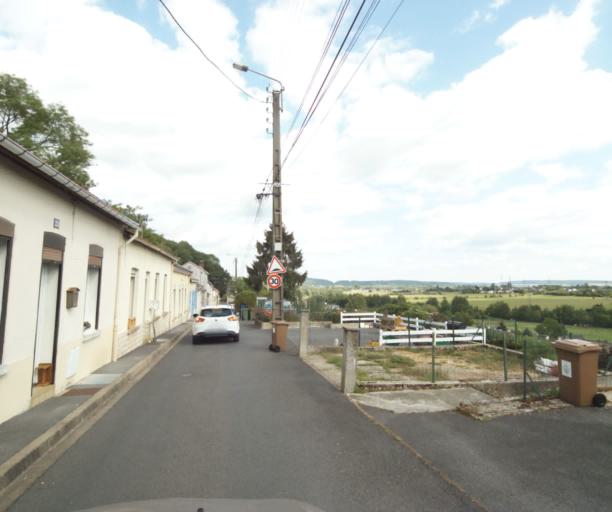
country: FR
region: Champagne-Ardenne
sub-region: Departement des Ardennes
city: Montcy-Notre-Dame
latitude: 49.7596
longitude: 4.7393
